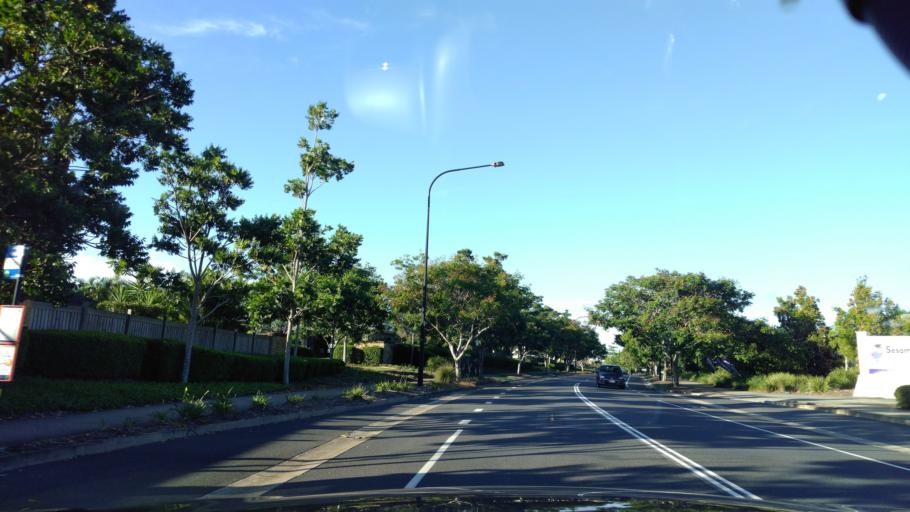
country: AU
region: Queensland
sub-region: Moreton Bay
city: Deception Bay
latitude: -27.2158
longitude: 153.0217
